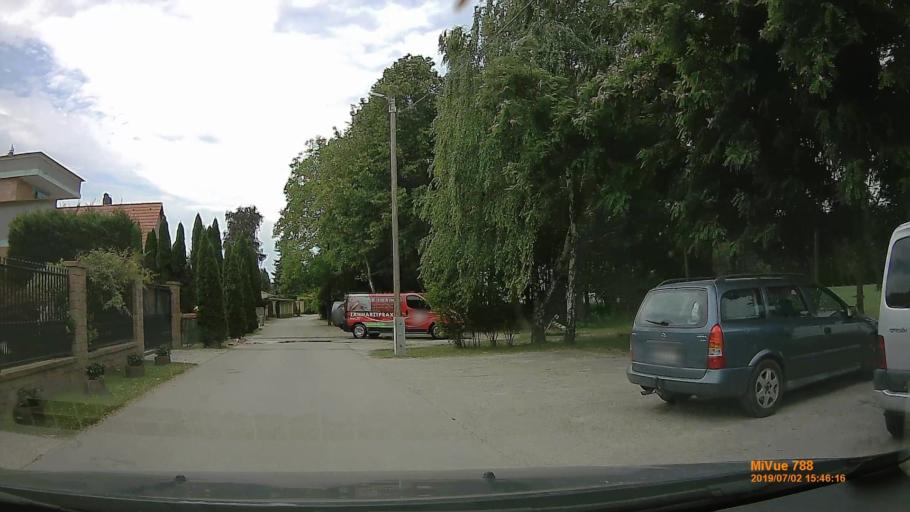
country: HU
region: Gyor-Moson-Sopron
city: Mosonmagyarovar
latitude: 47.8721
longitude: 17.2907
